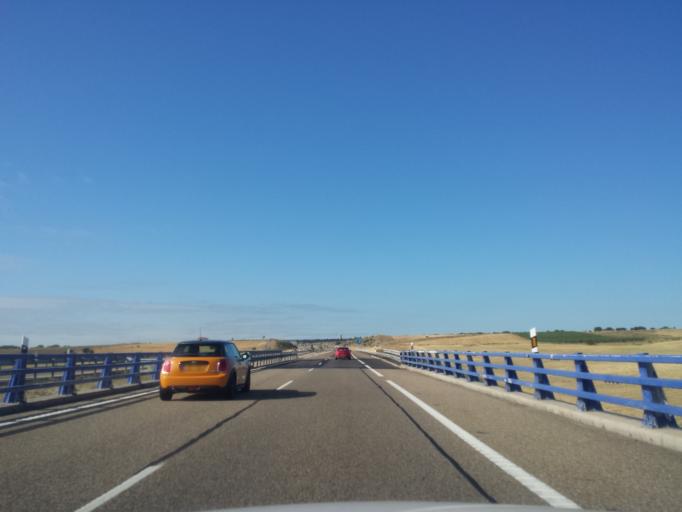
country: ES
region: Castille and Leon
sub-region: Provincia de Leon
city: Valdevimbre
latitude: 42.4101
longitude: -5.5893
